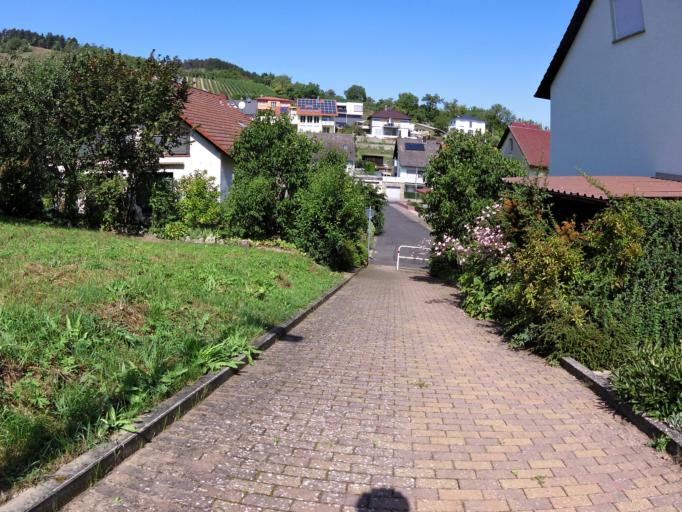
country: DE
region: Bavaria
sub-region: Regierungsbezirk Unterfranken
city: Erlabrunn
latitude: 49.8579
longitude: 9.8379
